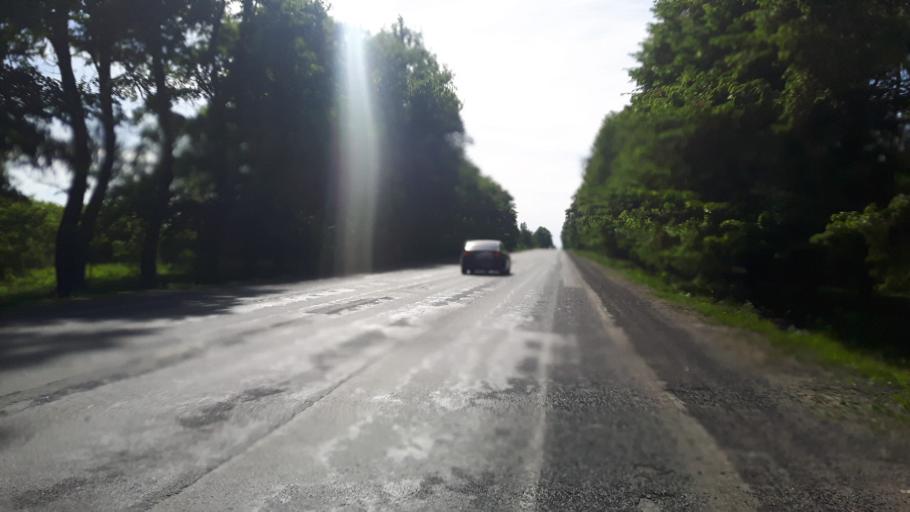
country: RU
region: Leningrad
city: Ivangorod
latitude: 59.3819
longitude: 28.3541
